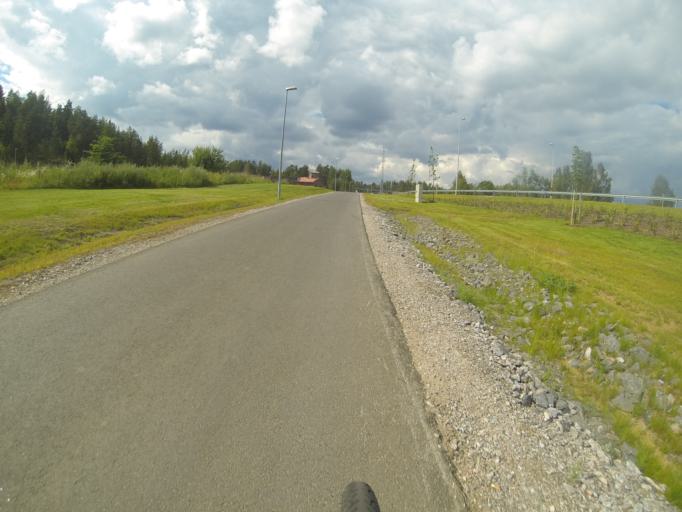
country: FI
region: Southern Savonia
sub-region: Savonlinna
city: Savonlinna
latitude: 61.8764
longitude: 28.8744
